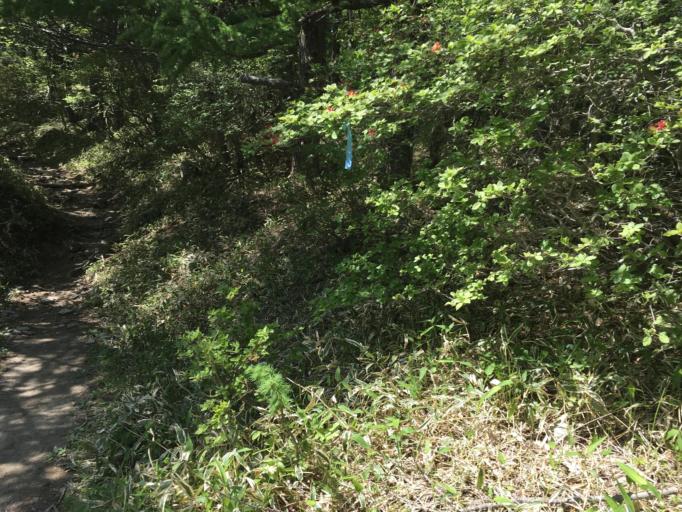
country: JP
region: Iwate
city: Ofunato
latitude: 39.1831
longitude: 141.7381
